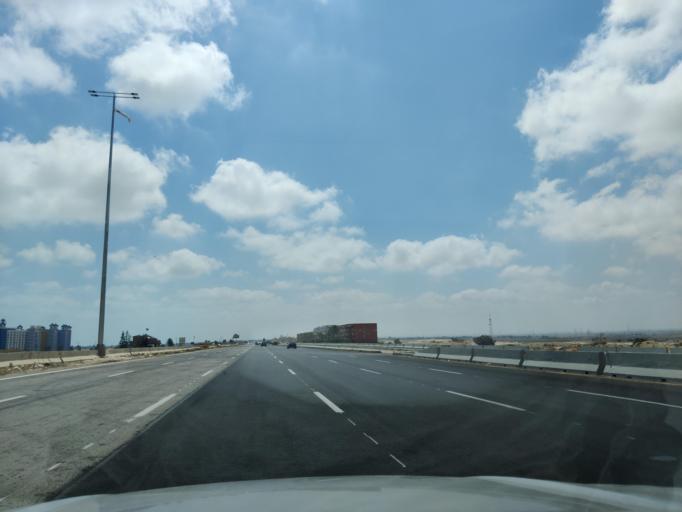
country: EG
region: Muhafazat Matruh
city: Al `Alamayn
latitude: 30.8225
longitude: 28.9947
